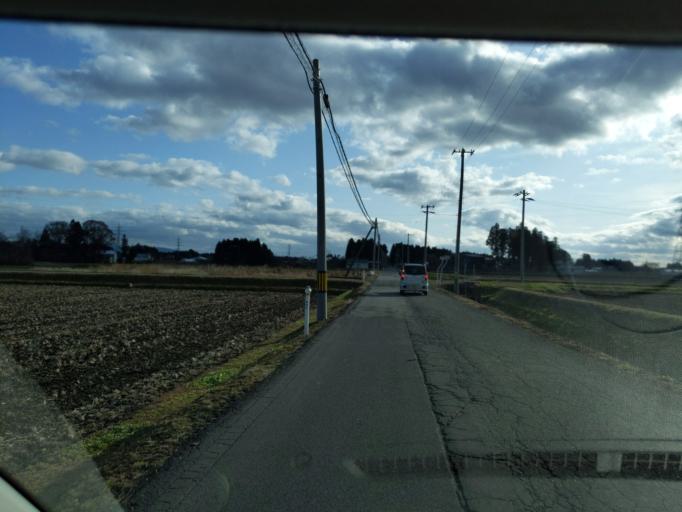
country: JP
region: Iwate
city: Mizusawa
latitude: 39.1326
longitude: 141.0805
